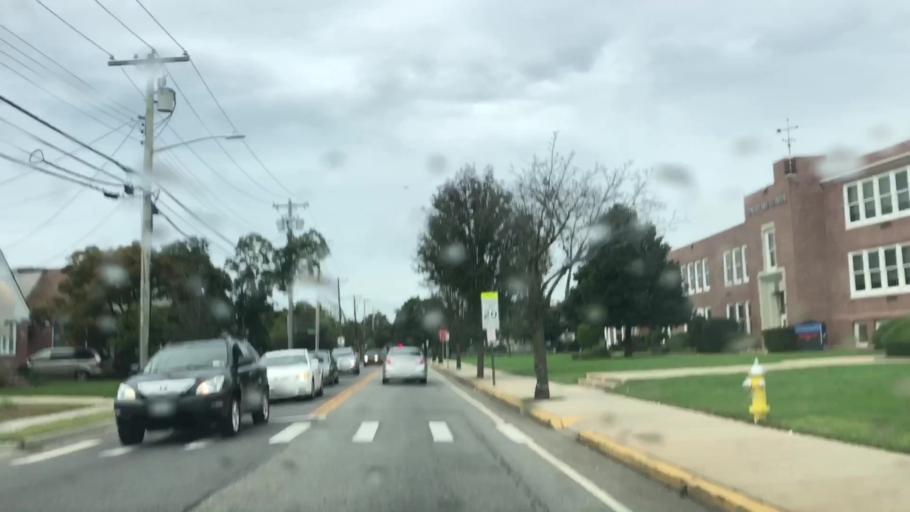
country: US
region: New York
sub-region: Nassau County
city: Stewart Manor
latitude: 40.7107
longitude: -73.6901
